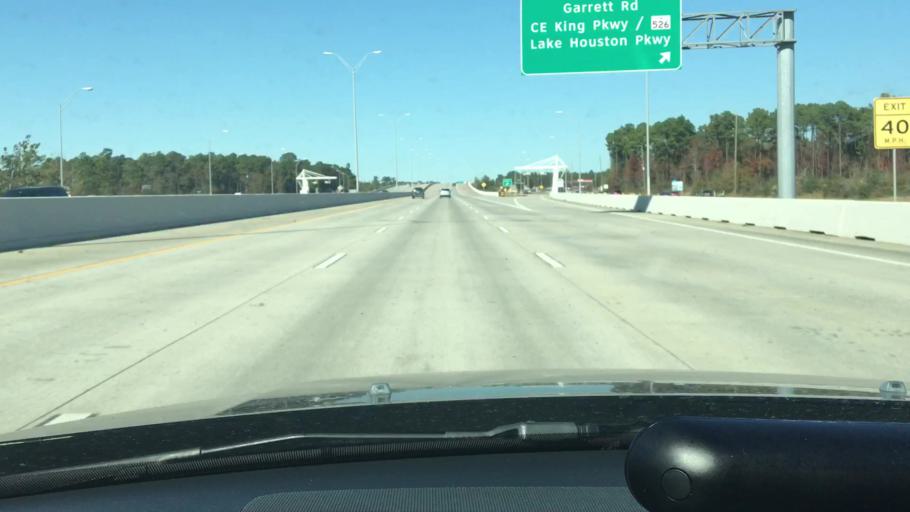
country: US
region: Texas
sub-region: Harris County
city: Sheldon
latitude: 29.8783
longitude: -95.1935
